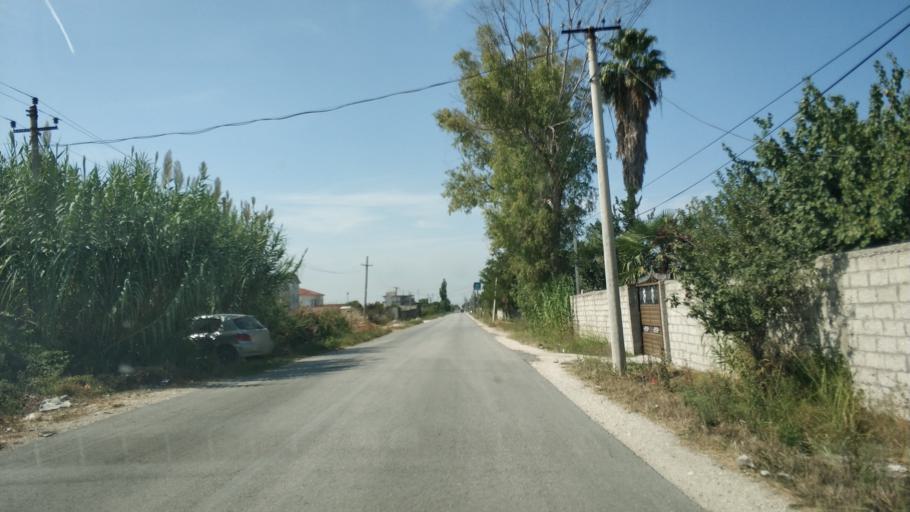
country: AL
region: Fier
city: Fier
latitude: 40.7307
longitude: 19.5403
